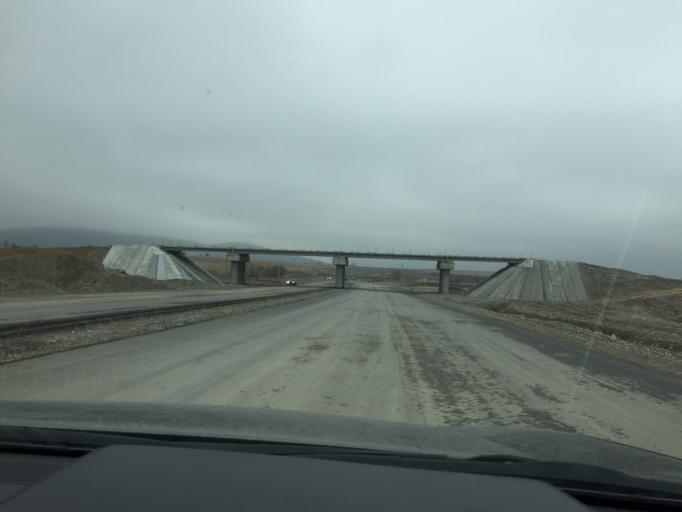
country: KZ
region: Ongtustik Qazaqstan
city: Kokterek
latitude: 42.5461
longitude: 70.2540
